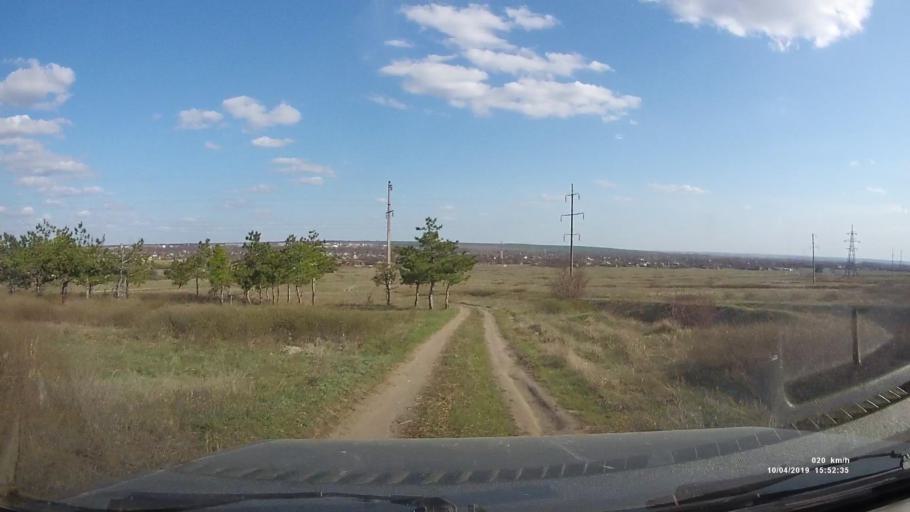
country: RU
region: Rostov
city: Masalovka
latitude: 48.4194
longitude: 40.2569
